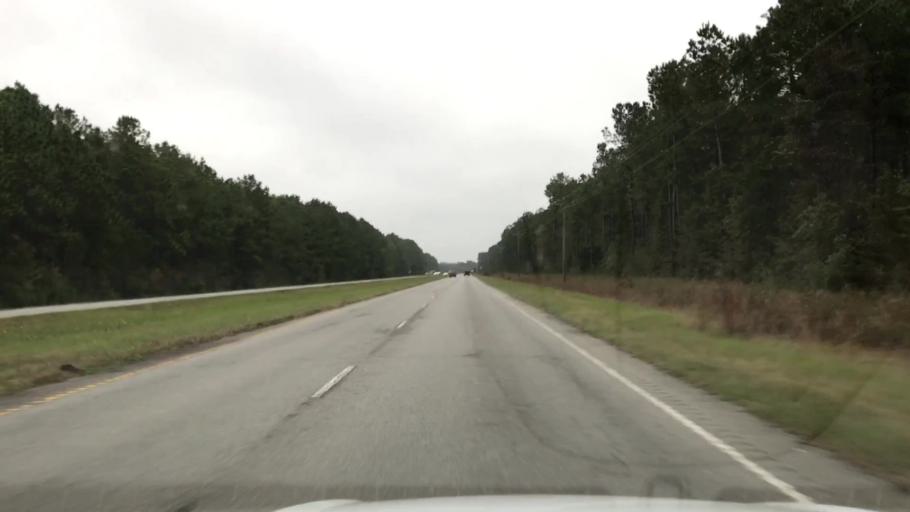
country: US
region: South Carolina
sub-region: Charleston County
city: Awendaw
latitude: 33.0180
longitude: -79.6337
